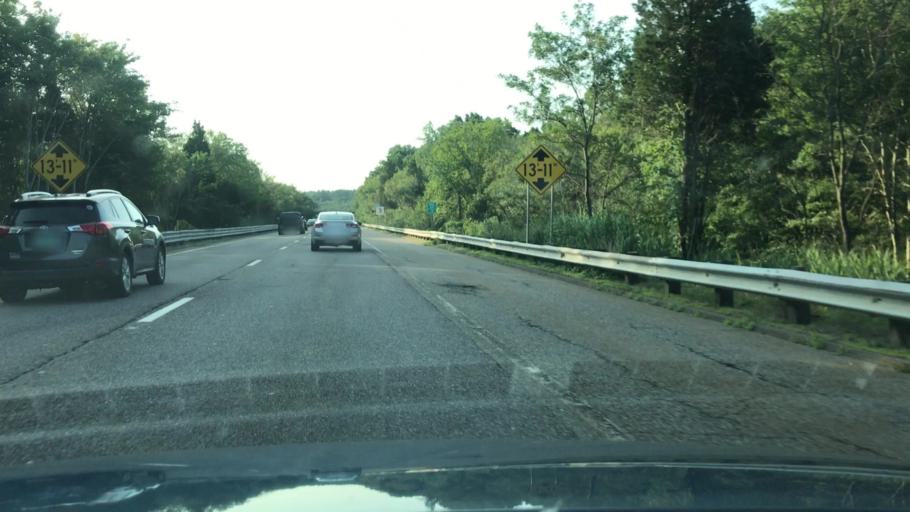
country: US
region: Massachusetts
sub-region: Plymouth County
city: Hanover
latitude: 42.1288
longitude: -70.8046
